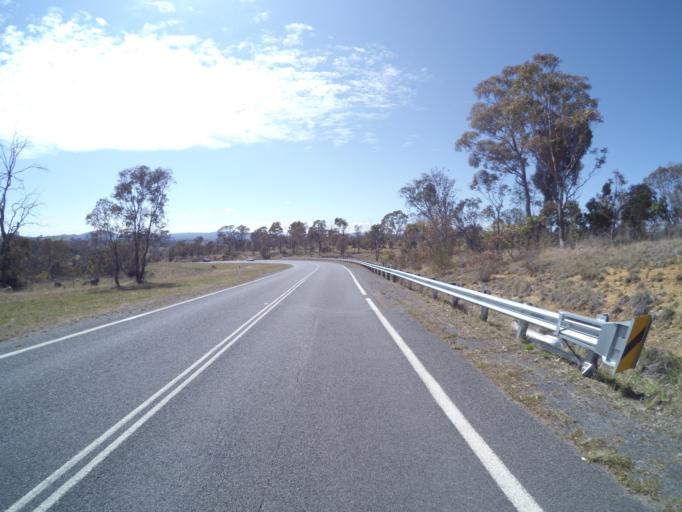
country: AU
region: Australian Capital Territory
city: Macarthur
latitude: -35.4604
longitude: 149.0355
